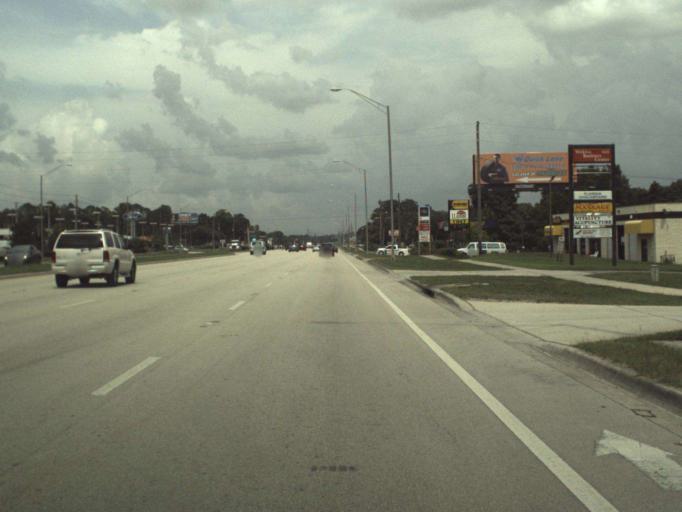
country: US
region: Florida
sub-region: Orange County
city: South Apopka
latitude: 28.6728
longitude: -81.4845
